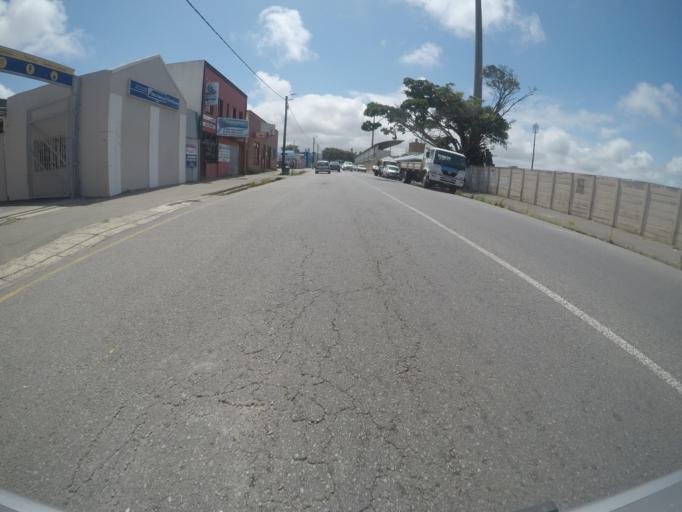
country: ZA
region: Eastern Cape
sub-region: Buffalo City Metropolitan Municipality
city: East London
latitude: -33.0081
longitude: 27.9057
